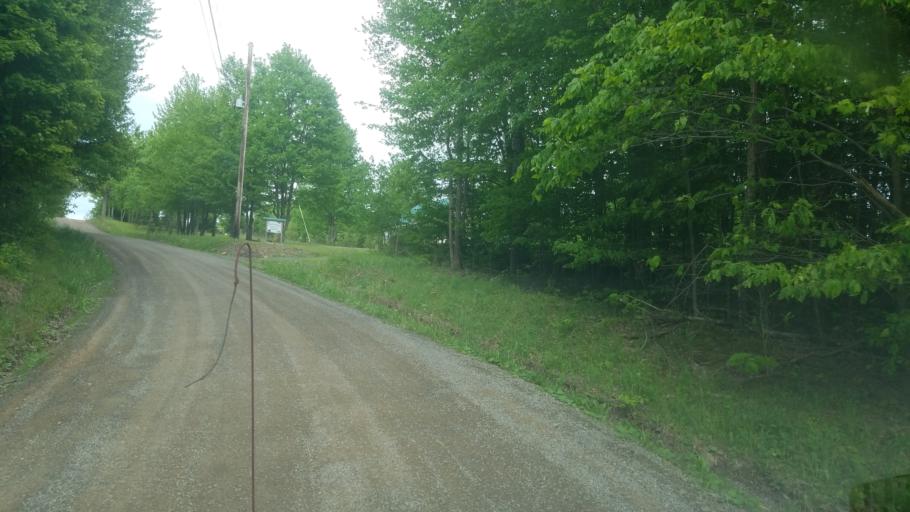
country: US
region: Pennsylvania
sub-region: Tioga County
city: Westfield
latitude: 41.9196
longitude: -77.7144
